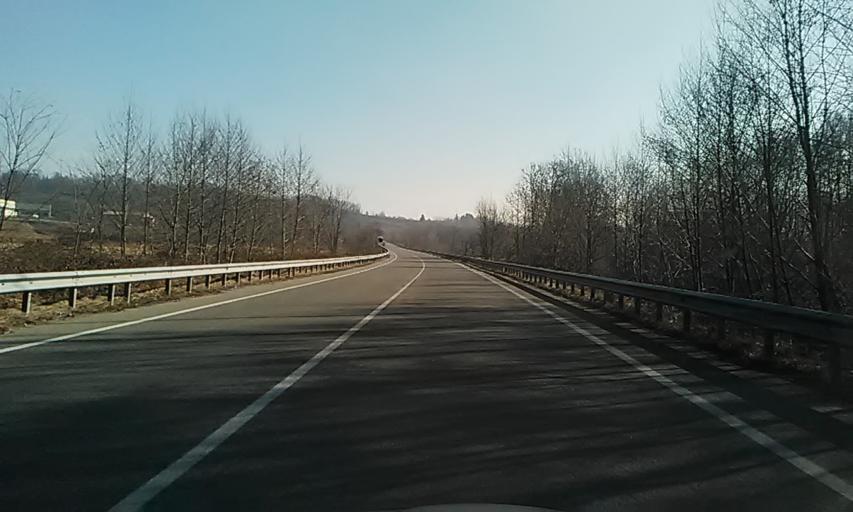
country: IT
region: Piedmont
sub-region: Provincia di Novara
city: Prato Sesia
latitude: 45.6603
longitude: 8.3713
